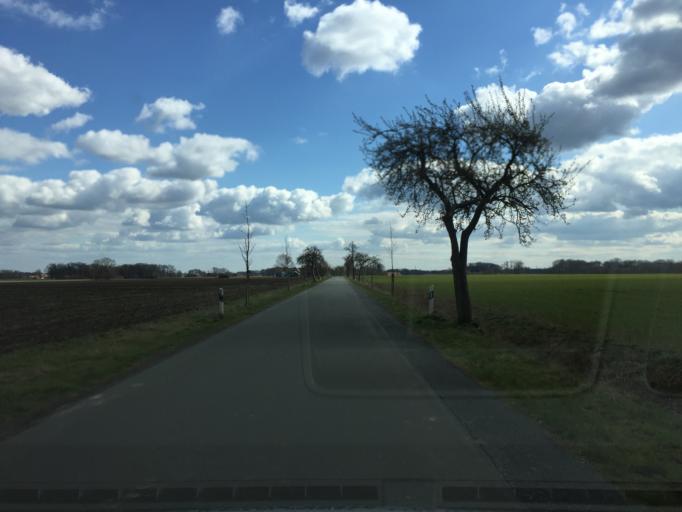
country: DE
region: Lower Saxony
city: Engeln
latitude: 52.7685
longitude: 8.9297
